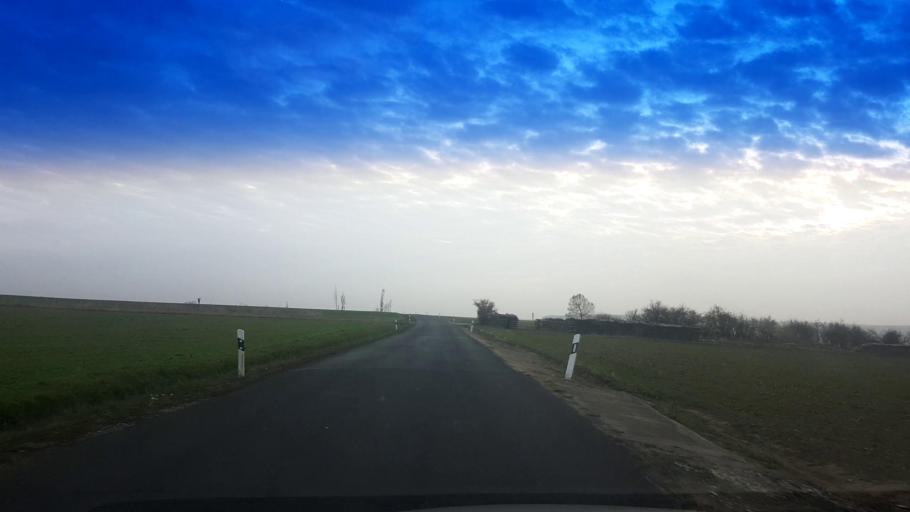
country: DE
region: Bavaria
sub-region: Upper Franconia
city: Priesendorf
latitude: 49.9065
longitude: 10.7358
